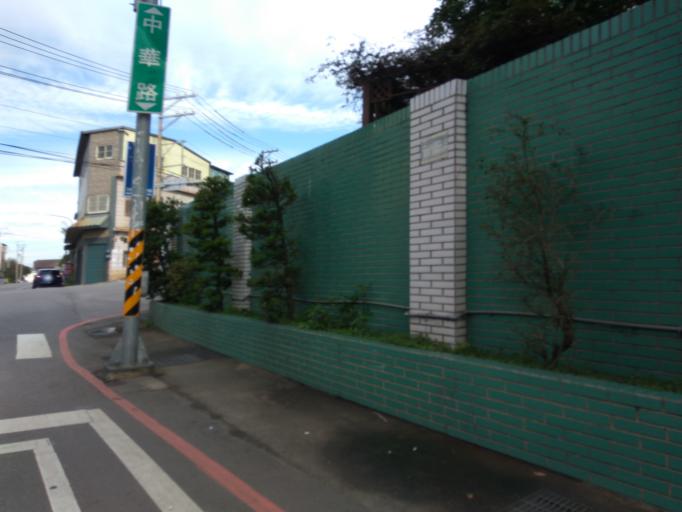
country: TW
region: Taiwan
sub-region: Hsinchu
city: Zhubei
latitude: 24.9843
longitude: 121.1060
